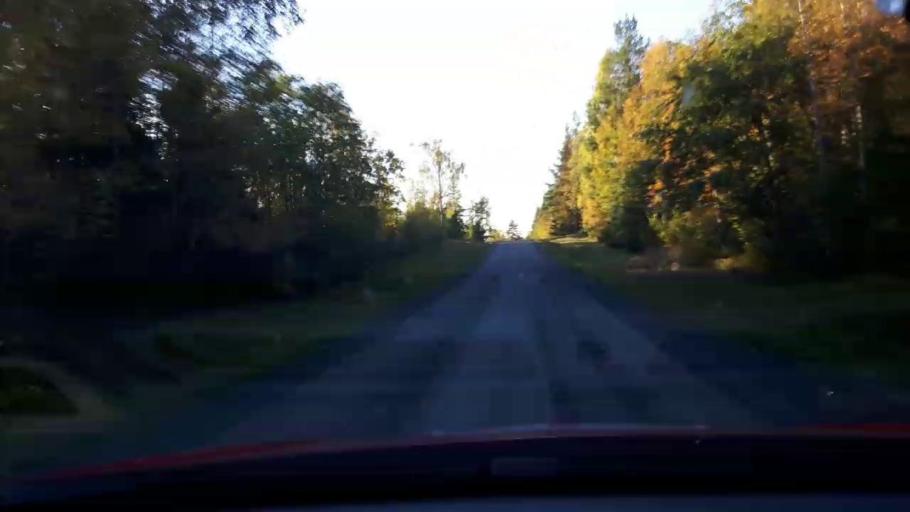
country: SE
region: Jaemtland
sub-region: Krokoms Kommun
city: Krokom
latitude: 63.4161
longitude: 14.6147
